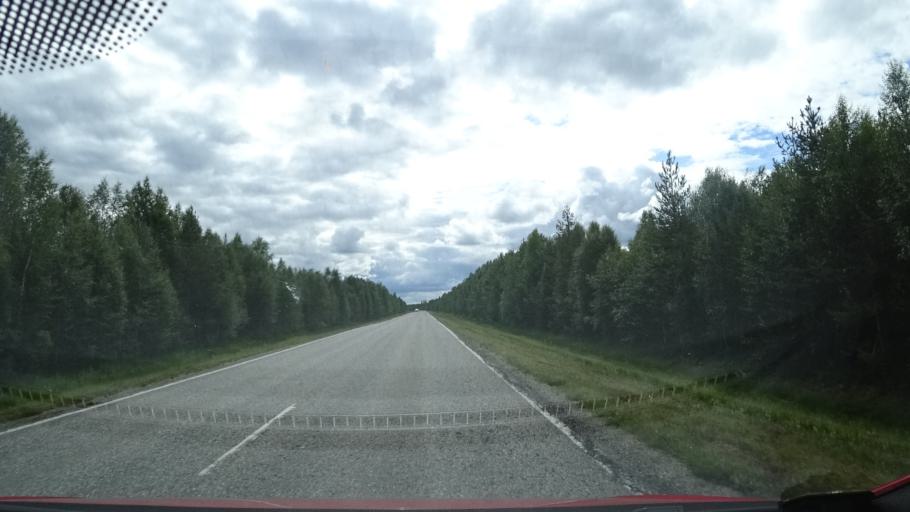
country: FI
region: Lapland
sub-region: Tunturi-Lappi
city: Kittilae
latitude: 67.4617
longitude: 24.9484
